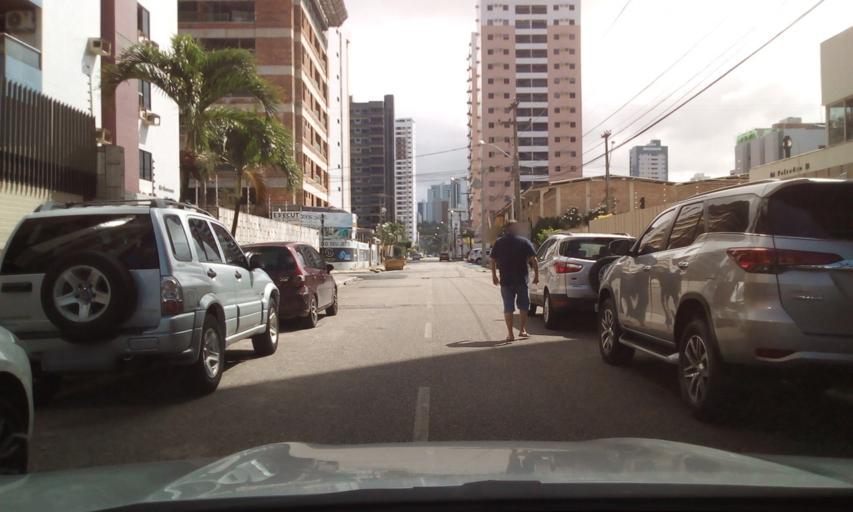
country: BR
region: Paraiba
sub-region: Joao Pessoa
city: Joao Pessoa
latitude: -7.1092
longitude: -34.8282
